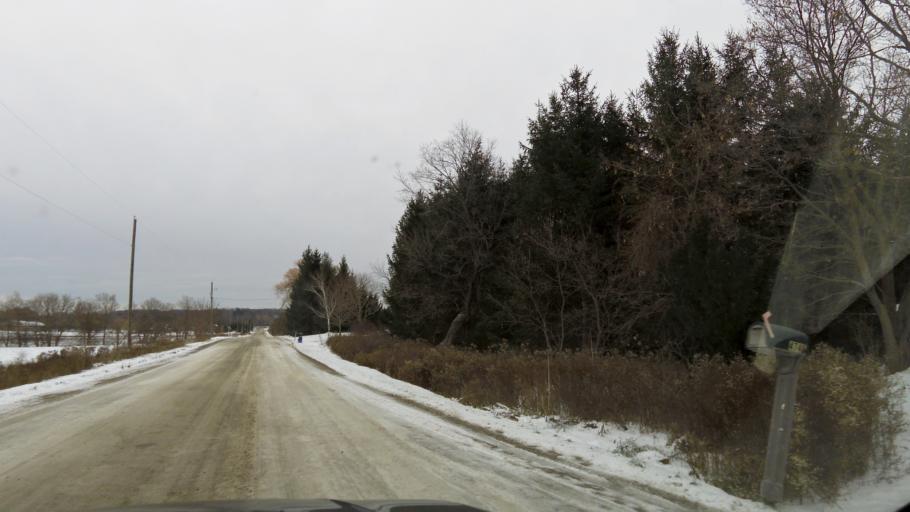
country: CA
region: Ontario
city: Bradford West Gwillimbury
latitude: 43.9832
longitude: -79.6289
